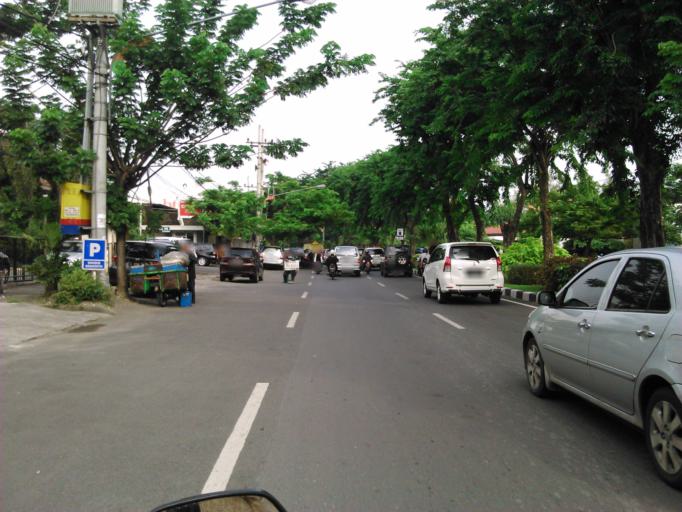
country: ID
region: East Java
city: Brongkalan
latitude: -7.2674
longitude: 112.7703
